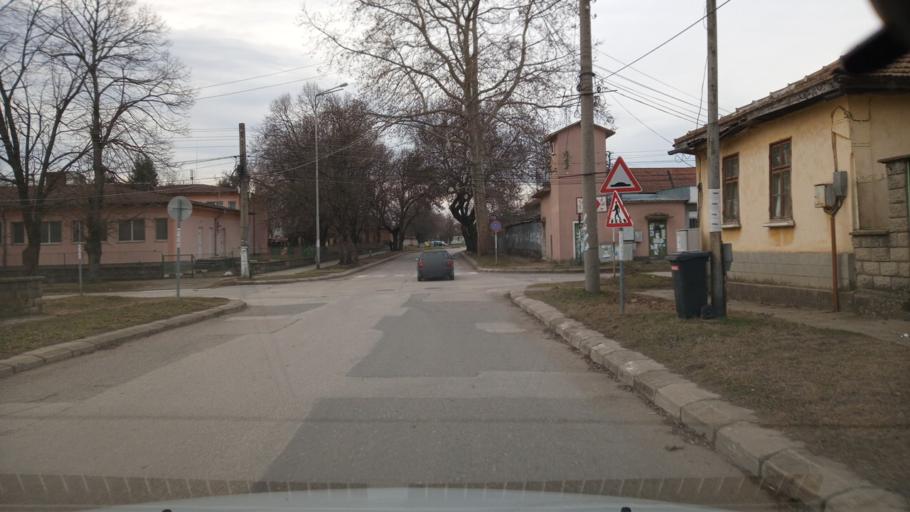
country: BG
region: Pleven
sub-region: Obshtina Belene
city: Belene
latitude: 43.6450
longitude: 25.1220
